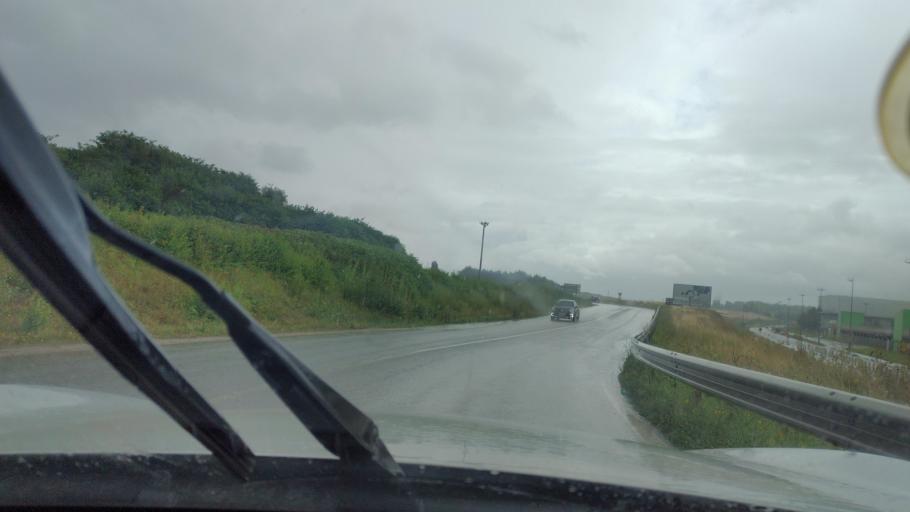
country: FR
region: Ile-de-France
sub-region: Departement de Seine-et-Marne
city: Mitry-Mory
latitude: 49.0128
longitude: 2.5899
